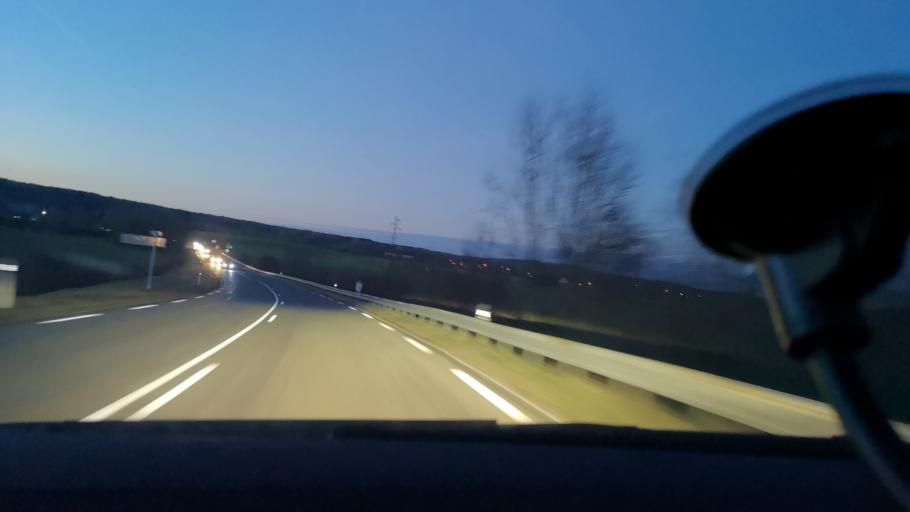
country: FR
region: Franche-Comte
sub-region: Departement du Jura
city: Champagnole
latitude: 46.7758
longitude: 5.9047
